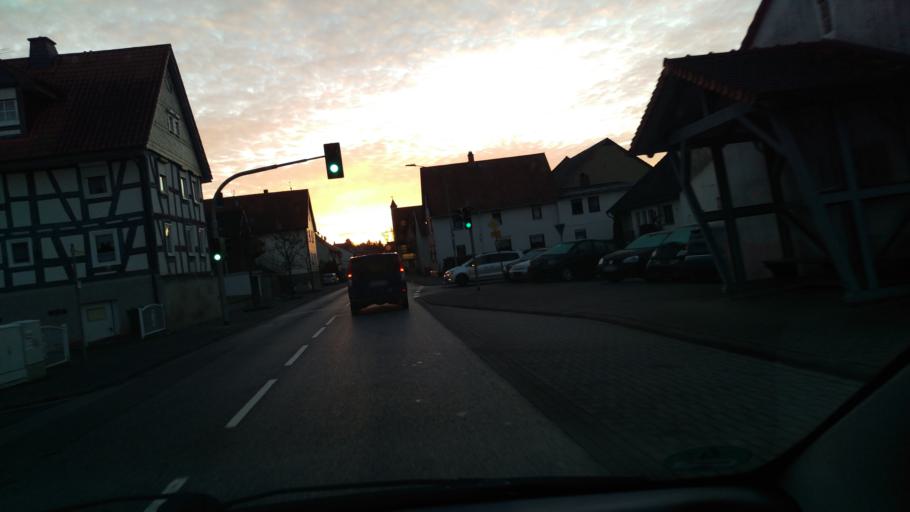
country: DE
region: Hesse
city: Kirtorf
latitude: 50.7692
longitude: 9.1006
